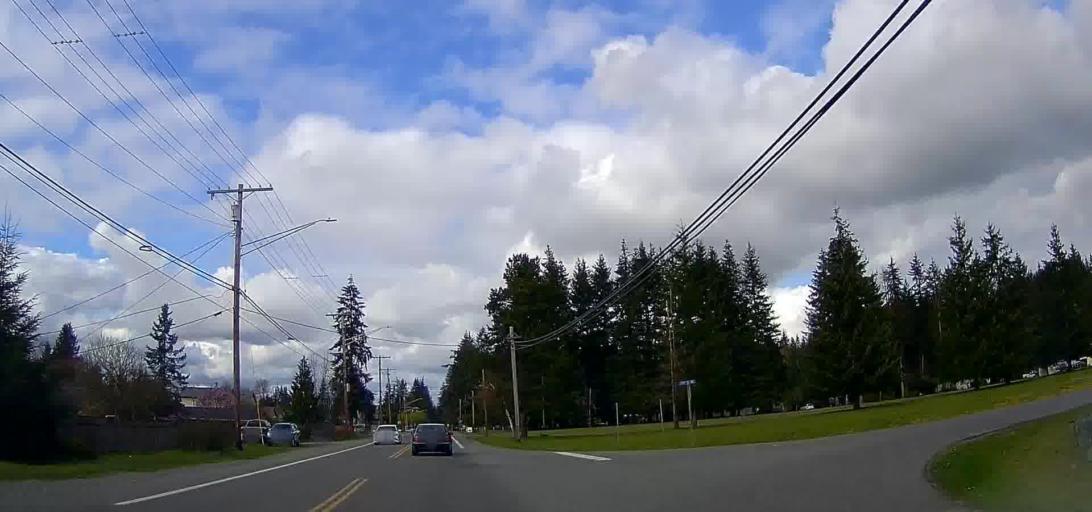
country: US
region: Washington
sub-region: Snohomish County
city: Smokey Point
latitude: 48.1583
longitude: -122.1829
